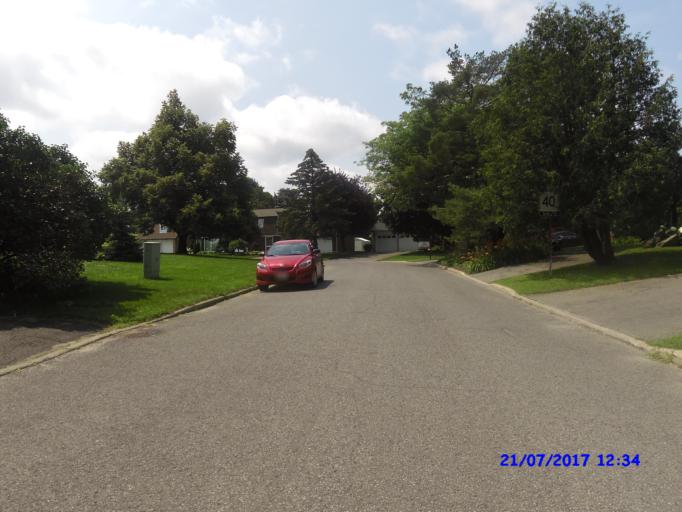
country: CA
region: Ontario
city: Ottawa
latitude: 45.3583
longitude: -75.7295
